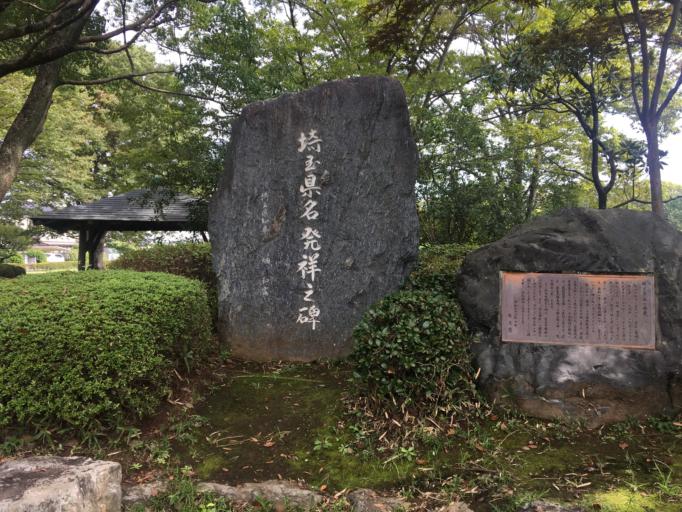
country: JP
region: Saitama
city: Gyoda
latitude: 36.1251
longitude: 139.4762
